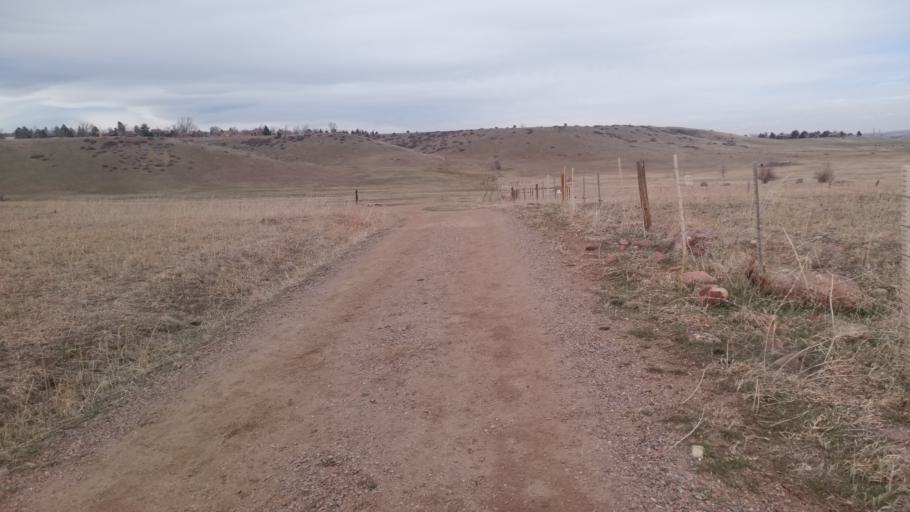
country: US
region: Colorado
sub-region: Boulder County
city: Boulder
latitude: 39.9599
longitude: -105.2460
